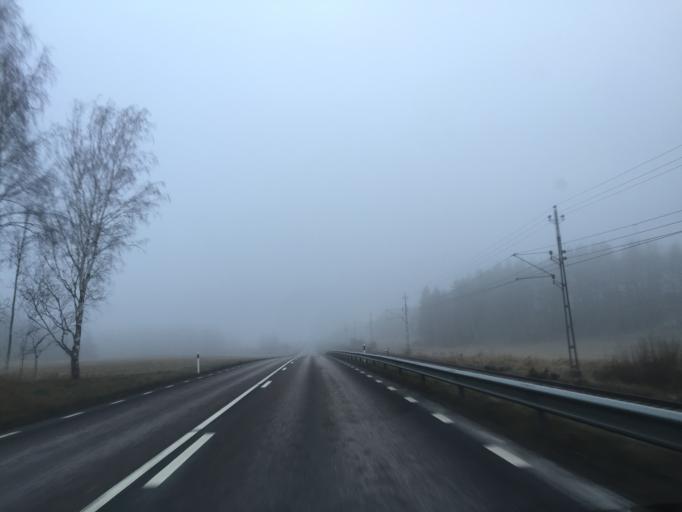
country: SE
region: Soedermanland
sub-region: Nykopings Kommun
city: Olstorp
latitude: 58.8828
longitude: 16.6648
